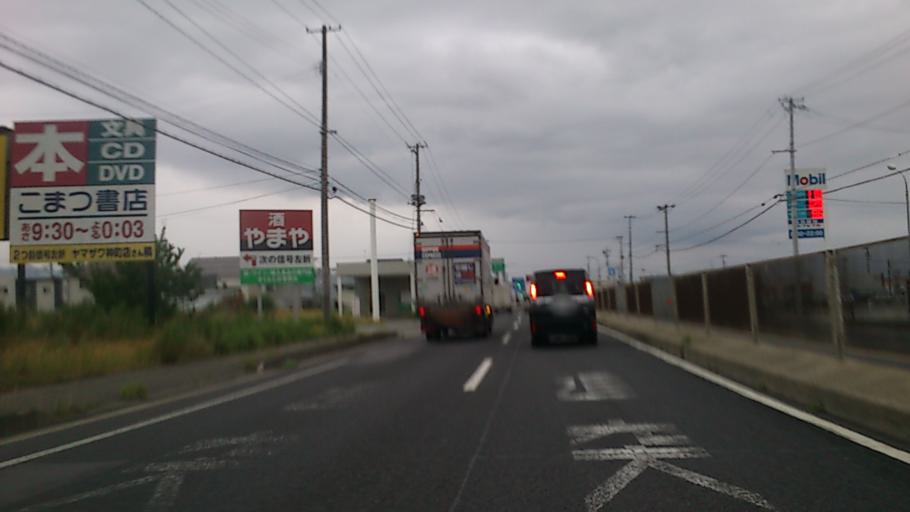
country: JP
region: Yamagata
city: Higashine
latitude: 38.4315
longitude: 140.3777
